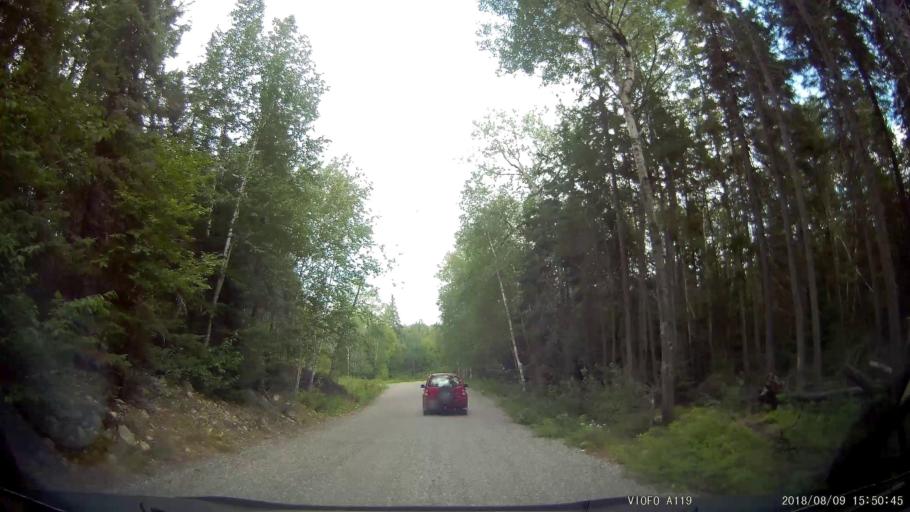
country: CA
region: Ontario
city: Rayside-Balfour
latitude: 46.5932
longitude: -81.5363
